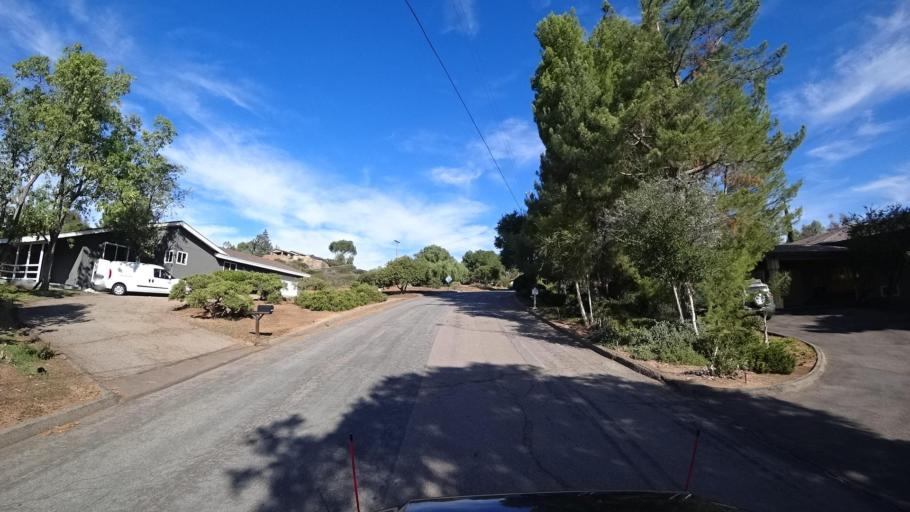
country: US
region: California
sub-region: San Diego County
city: Alpine
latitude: 32.8202
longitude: -116.7423
